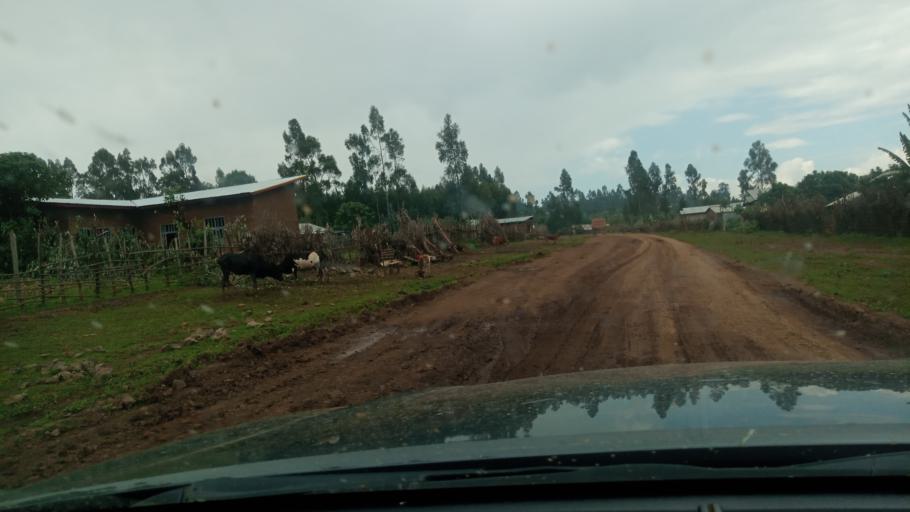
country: ET
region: Oromiya
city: Hagere Hiywet
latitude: 9.3188
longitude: 38.0673
